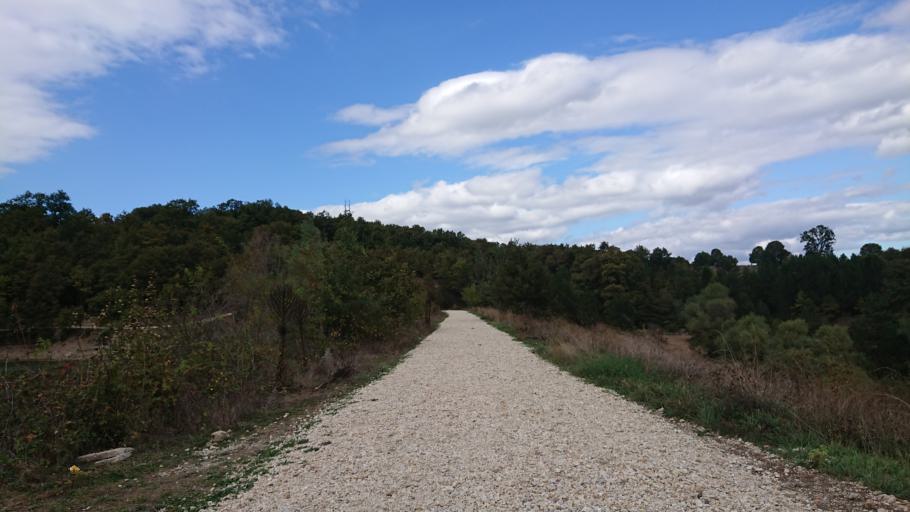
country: TR
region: Bilecik
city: Pazaryeri
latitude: 40.0162
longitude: 29.7971
